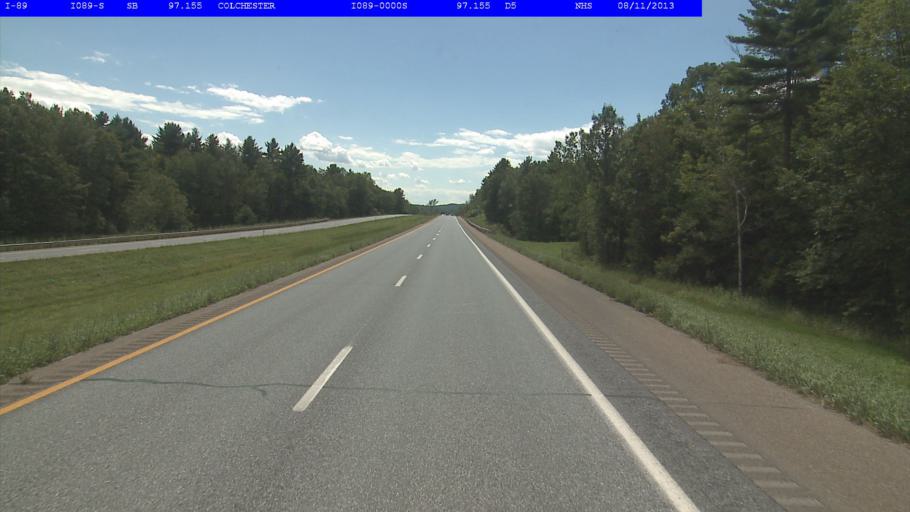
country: US
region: Vermont
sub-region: Chittenden County
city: Colchester
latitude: 44.5805
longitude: -73.1763
